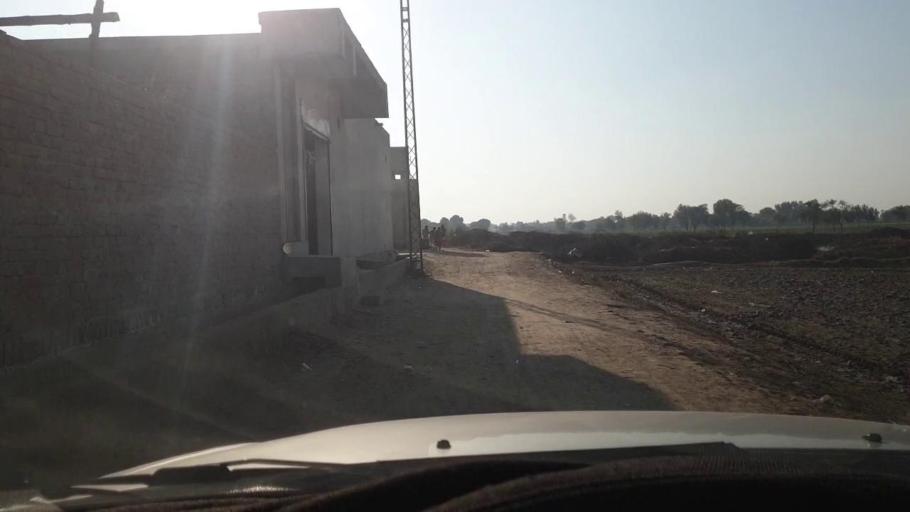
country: PK
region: Sindh
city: Mirpur Mathelo
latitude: 28.0200
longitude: 69.6042
